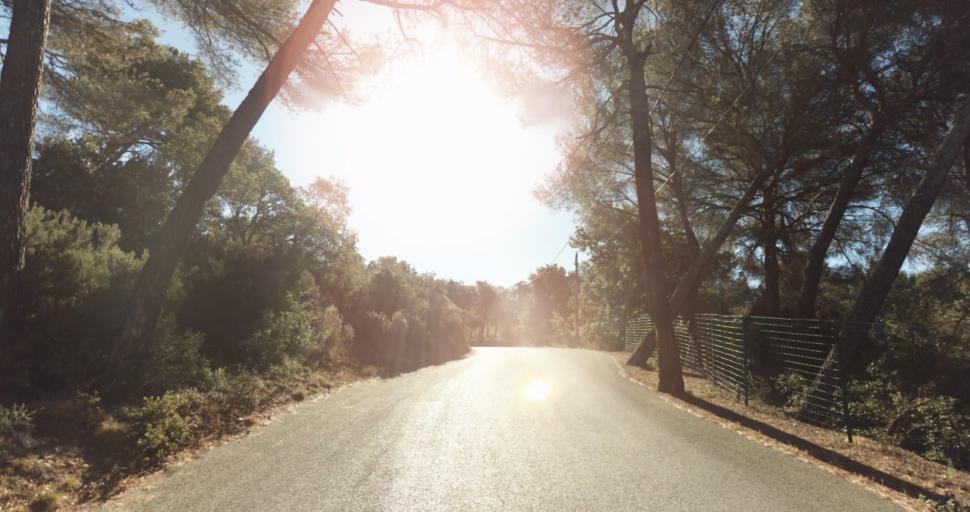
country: FR
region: Provence-Alpes-Cote d'Azur
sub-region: Departement du Var
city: Gassin
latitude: 43.2159
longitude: 6.5857
